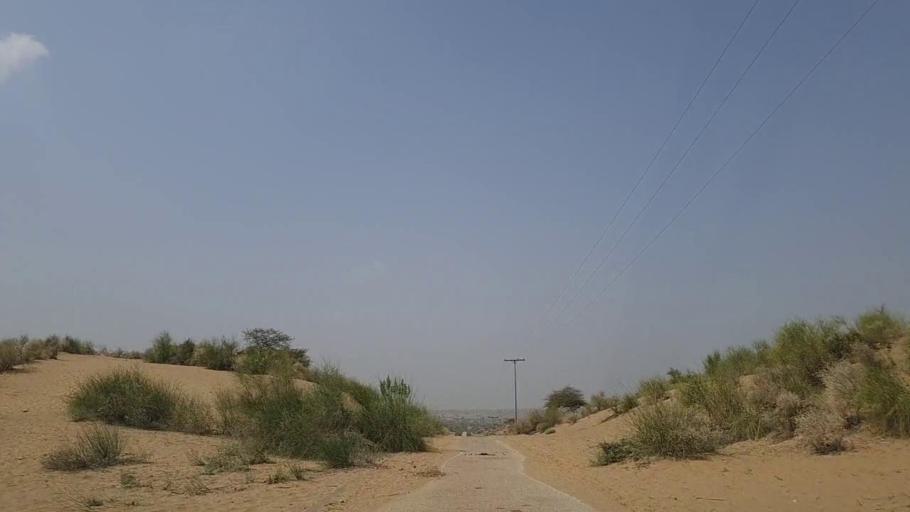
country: PK
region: Sindh
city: Mithi
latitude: 24.7694
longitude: 69.8921
